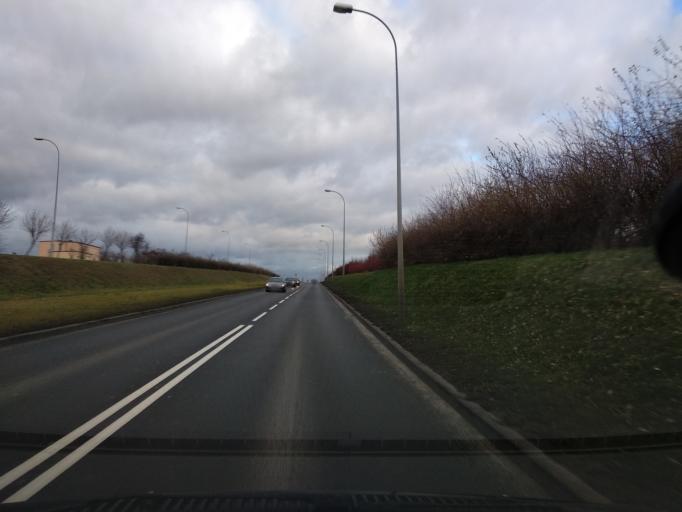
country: PL
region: Greater Poland Voivodeship
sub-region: Kalisz
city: Kalisz
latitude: 51.7797
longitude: 18.0811
